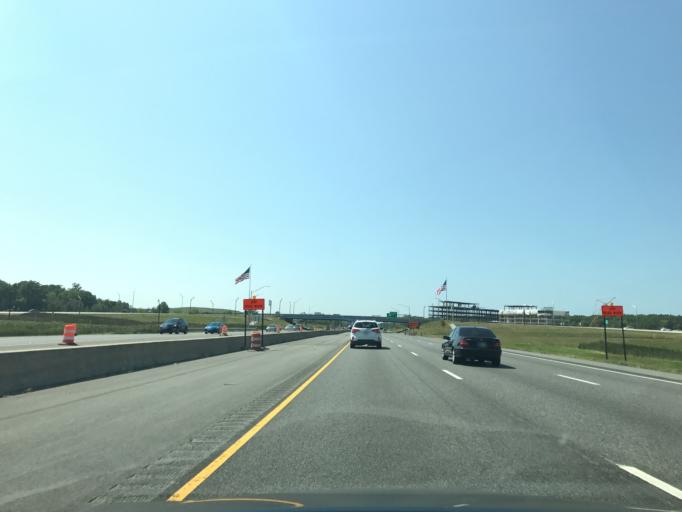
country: US
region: Indiana
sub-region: LaPorte County
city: Michigan City
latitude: 41.6584
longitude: -86.8900
